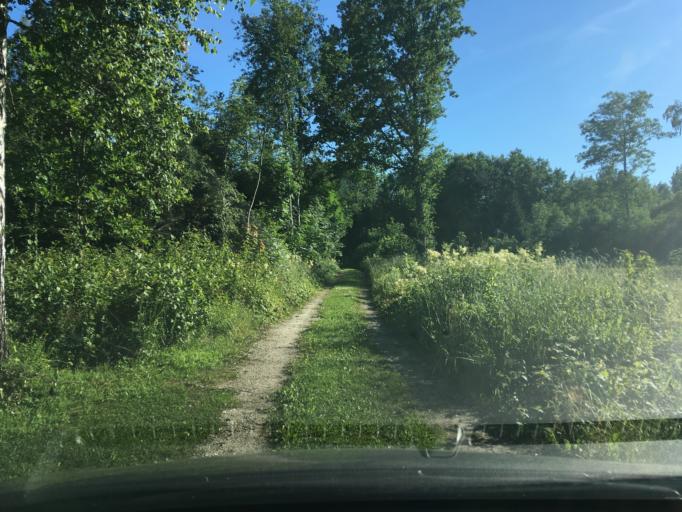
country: EE
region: Laeaene
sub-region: Lihula vald
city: Lihula
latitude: 58.5876
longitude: 23.7367
